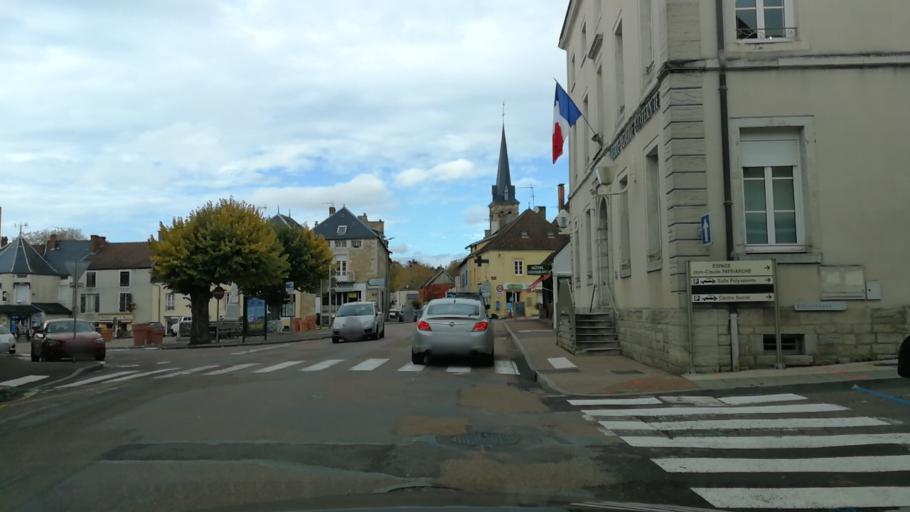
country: FR
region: Bourgogne
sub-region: Departement de la Cote-d'Or
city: Pouilly-en-Auxois
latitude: 47.2620
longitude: 4.5564
